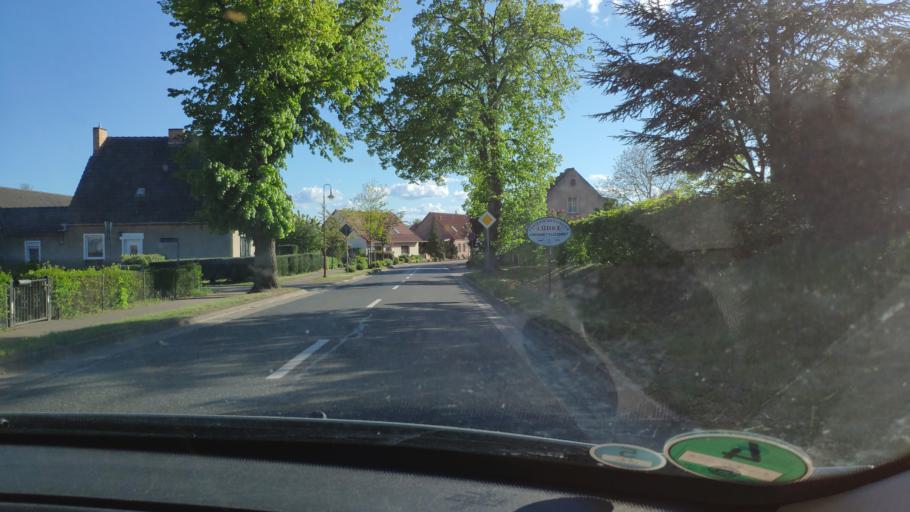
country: DE
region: Mecklenburg-Vorpommern
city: Wesenberg
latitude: 53.3408
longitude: 12.9828
